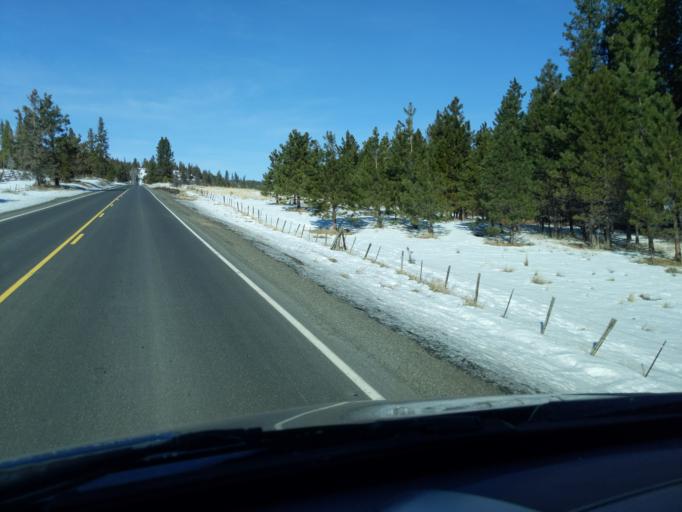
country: US
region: Oregon
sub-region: Grant County
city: John Day
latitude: 44.8968
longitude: -119.0144
